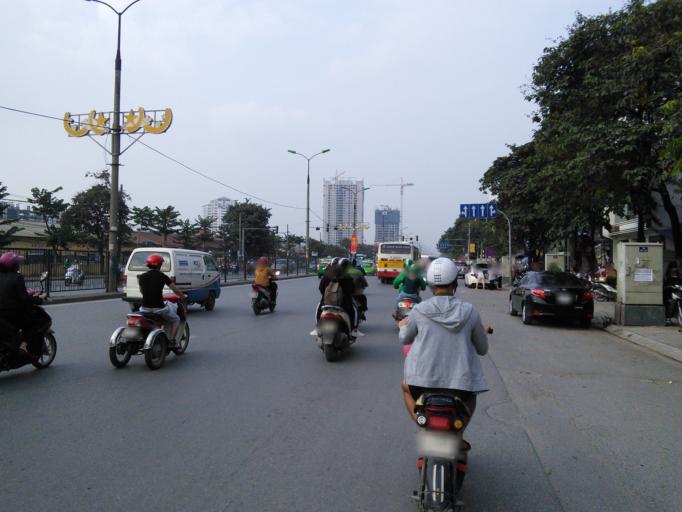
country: VN
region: Ha Noi
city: Van Dien
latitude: 20.9787
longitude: 105.8411
